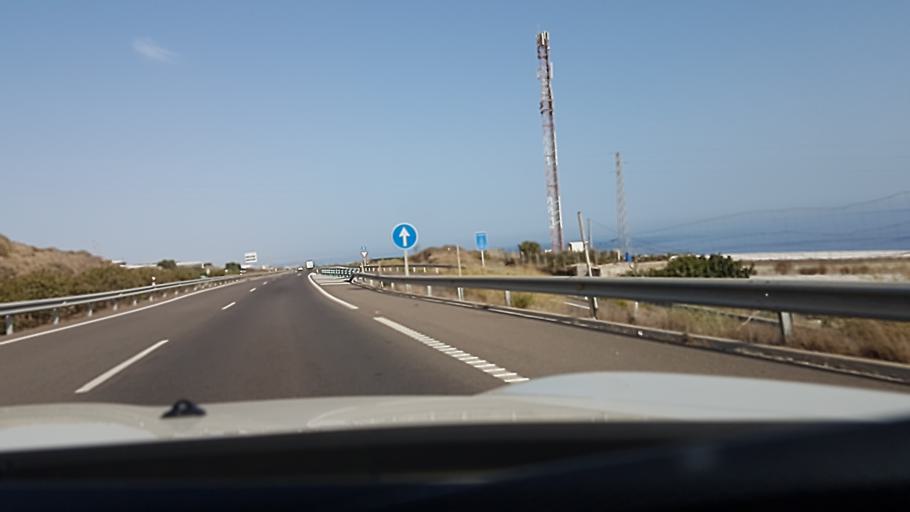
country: ES
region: Andalusia
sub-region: Provincia de Almeria
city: Adra
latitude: 36.7496
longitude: -3.0541
